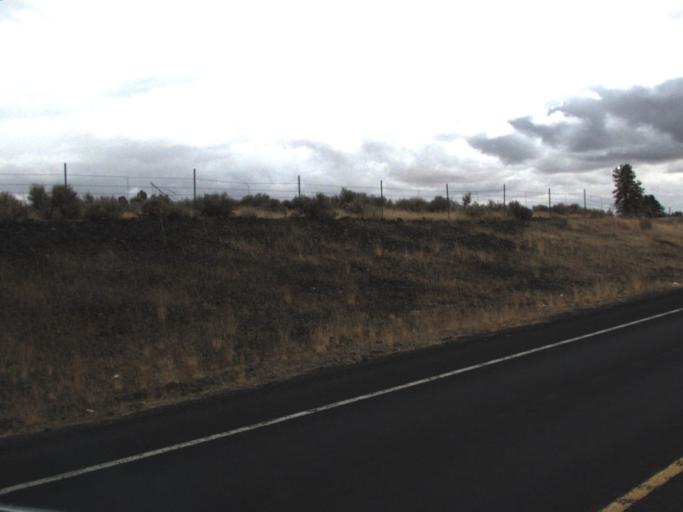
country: US
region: Washington
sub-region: Lincoln County
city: Davenport
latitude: 47.6704
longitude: -118.3627
